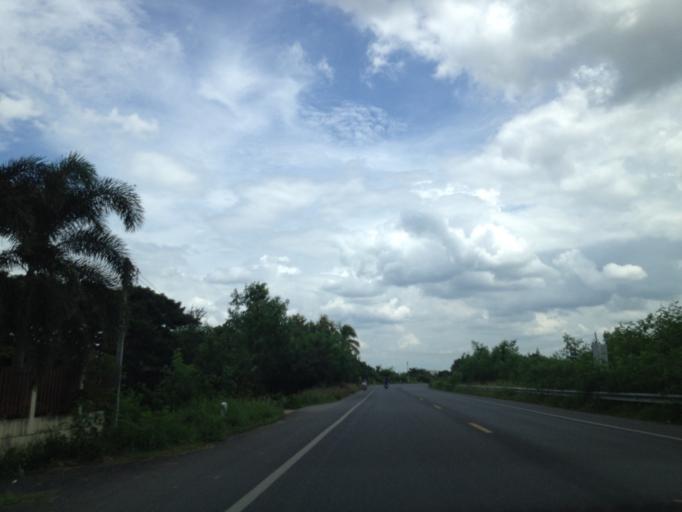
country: TH
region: Chiang Mai
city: San Pa Tong
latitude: 18.6308
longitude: 98.8805
